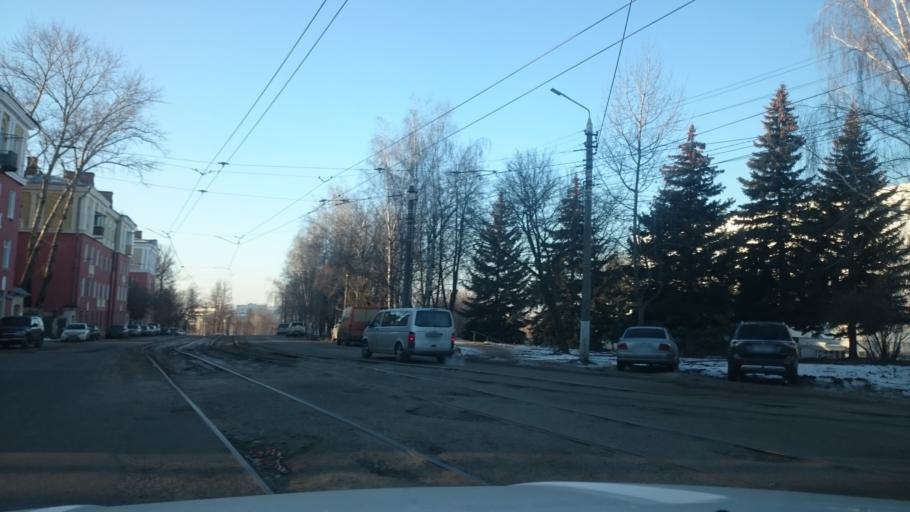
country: RU
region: Tula
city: Tula
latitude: 54.2092
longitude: 37.6568
